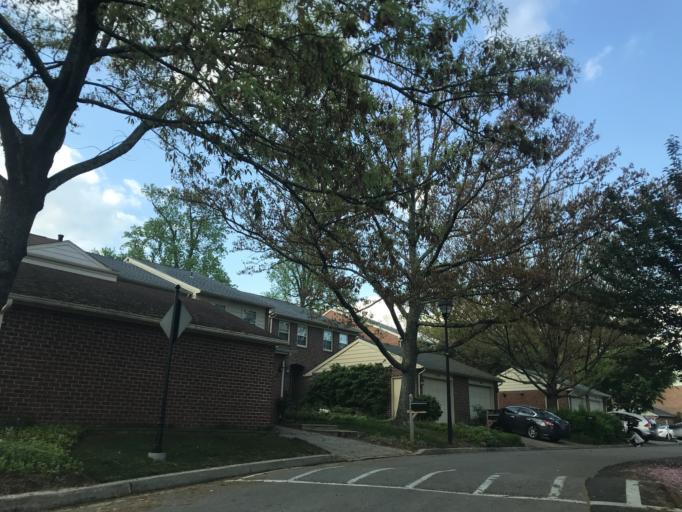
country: US
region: Maryland
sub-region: Baltimore County
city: Towson
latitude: 39.3757
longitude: -76.6222
